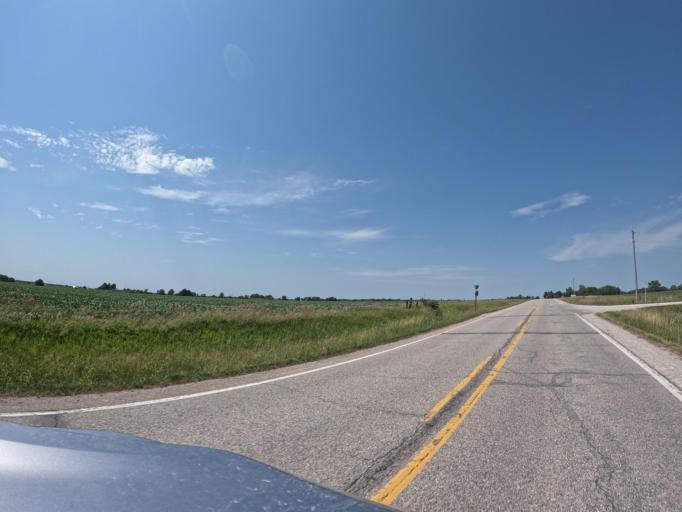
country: US
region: Iowa
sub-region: Henry County
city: Mount Pleasant
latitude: 40.8983
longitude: -91.6220
